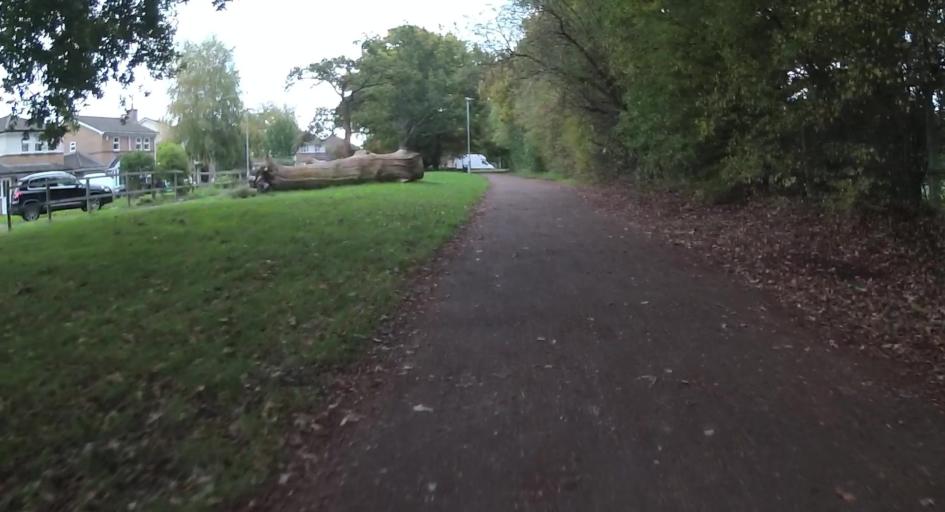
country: GB
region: England
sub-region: Bracknell Forest
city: Crowthorne
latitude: 51.3971
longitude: -0.7804
